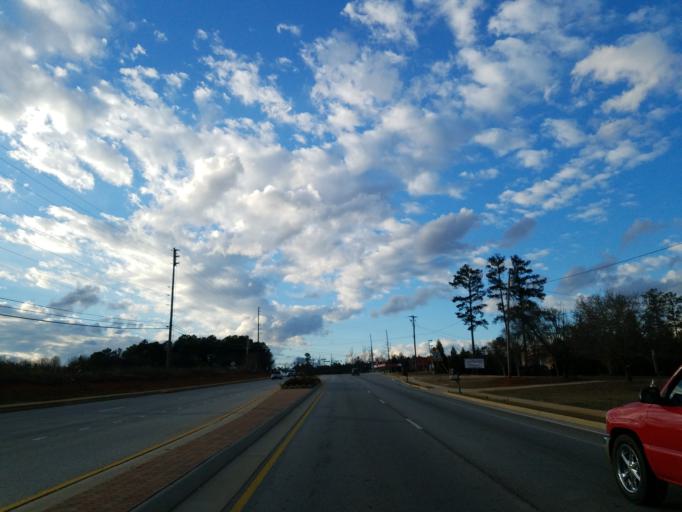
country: US
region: Georgia
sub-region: Henry County
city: McDonough
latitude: 33.4564
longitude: -84.1716
